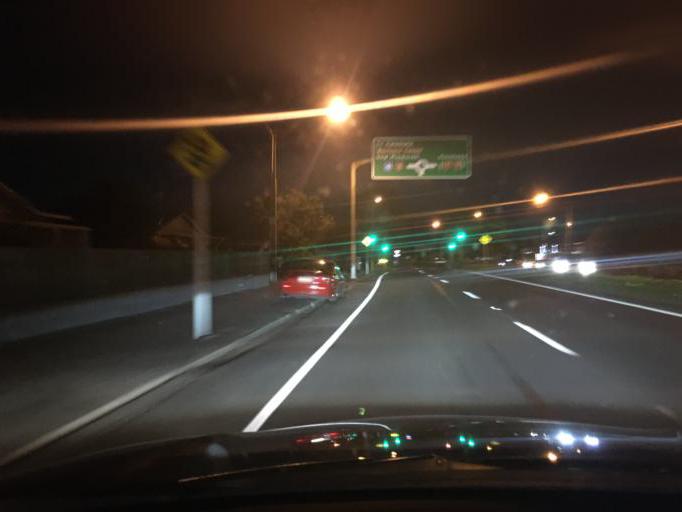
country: NZ
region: Waikato
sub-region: Hamilton City
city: Hamilton
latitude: -37.8111
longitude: 175.2835
